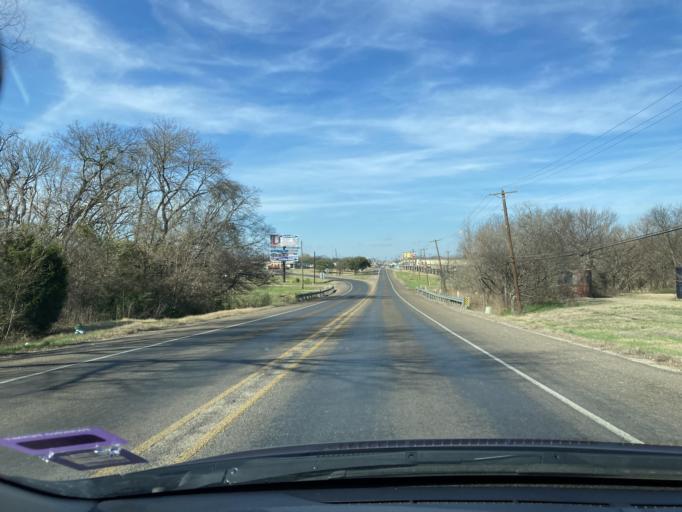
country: US
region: Texas
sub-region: Navarro County
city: Corsicana
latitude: 32.0820
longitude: -96.4509
